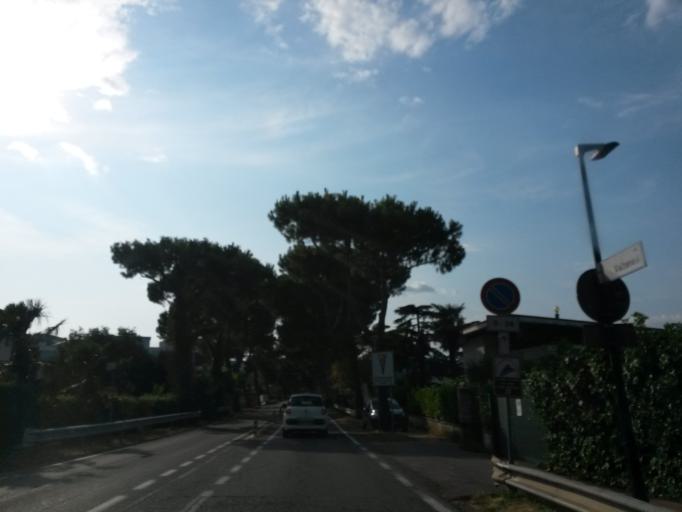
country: IT
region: Lombardy
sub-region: Provincia di Brescia
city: Padenghe sul Garda
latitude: 45.4900
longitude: 10.5239
